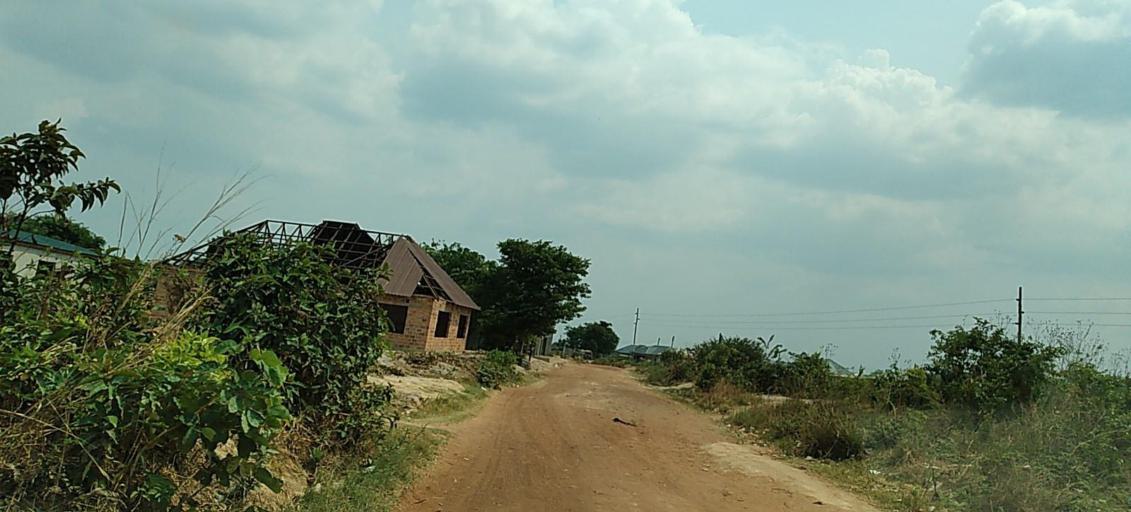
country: ZM
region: Copperbelt
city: Kalulushi
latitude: -12.8570
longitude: 28.0786
